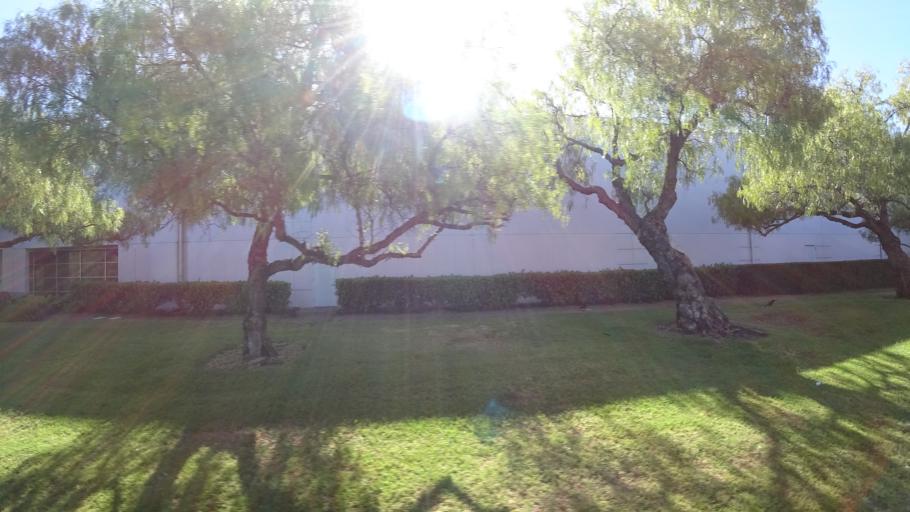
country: US
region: California
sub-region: Alameda County
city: Union City
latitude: 37.6166
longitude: -122.0525
